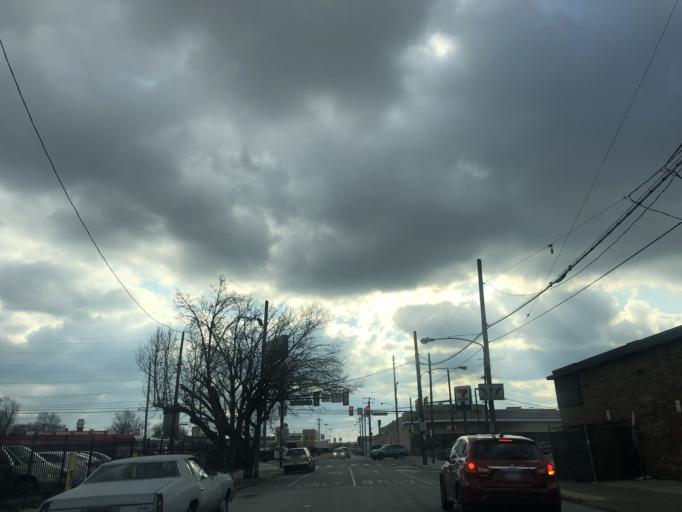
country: US
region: Pennsylvania
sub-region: Philadelphia County
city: Philadelphia
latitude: 39.9233
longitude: -75.1850
